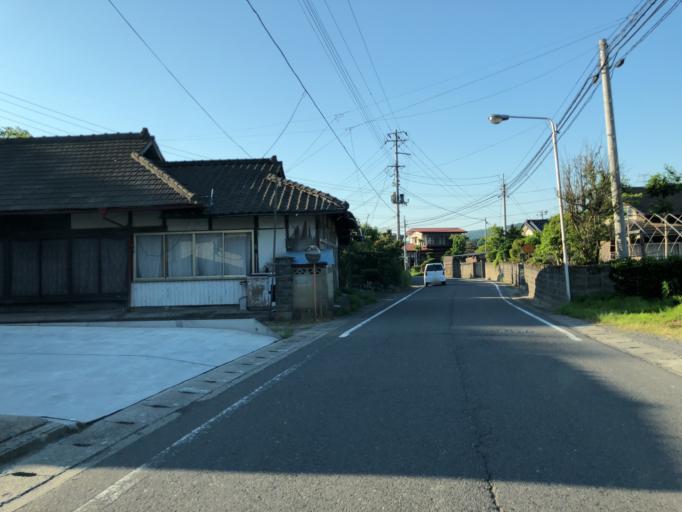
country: JP
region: Ibaraki
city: Daigo
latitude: 36.9426
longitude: 140.4409
